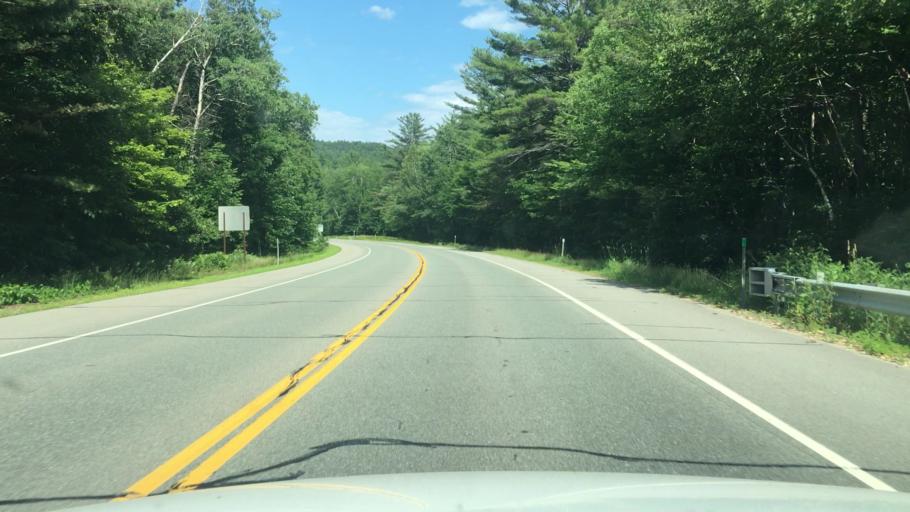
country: US
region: New Hampshire
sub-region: Coos County
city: Gorham
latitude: 44.3844
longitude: -71.0191
